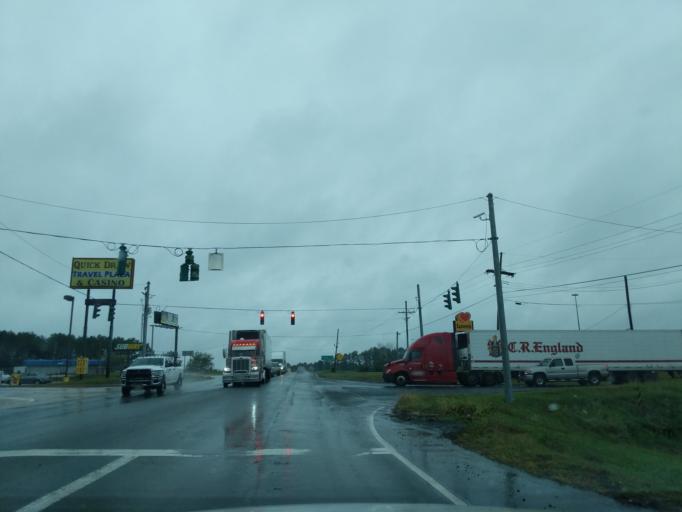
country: US
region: Louisiana
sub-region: Webster Parish
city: Minden
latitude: 32.5831
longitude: -93.2479
